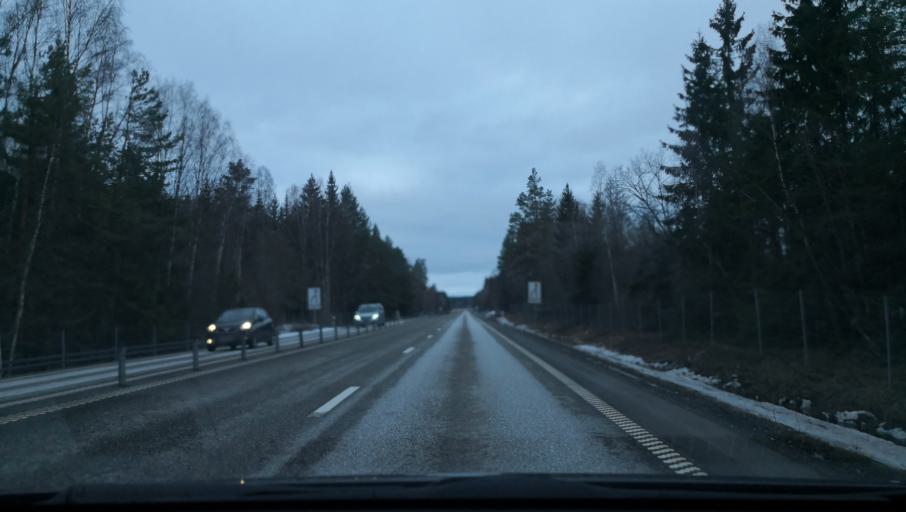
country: SE
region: Vaestmanland
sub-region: Surahammars Kommun
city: Surahammar
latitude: 59.7385
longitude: 16.2281
